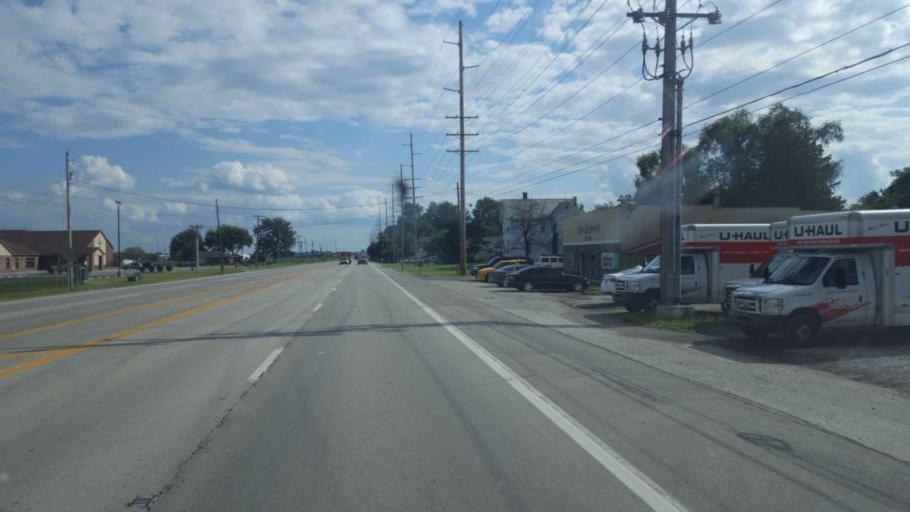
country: US
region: Ohio
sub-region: Wood County
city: Bowling Green
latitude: 41.4070
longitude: -83.6508
